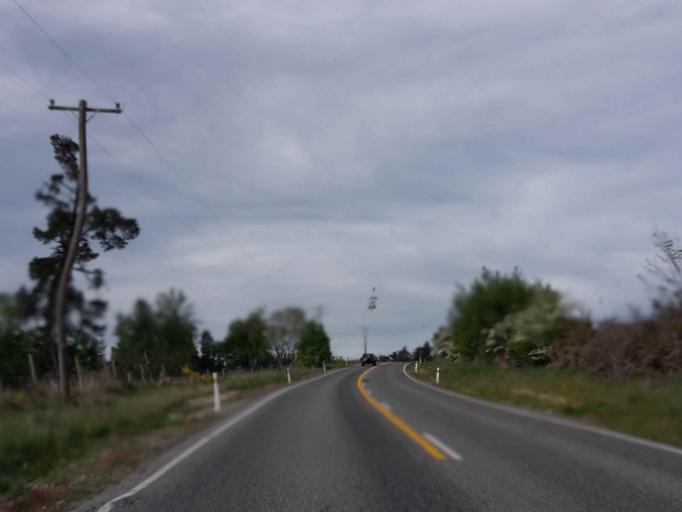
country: NZ
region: Canterbury
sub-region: Timaru District
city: Pleasant Point
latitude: -44.1277
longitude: 171.0920
